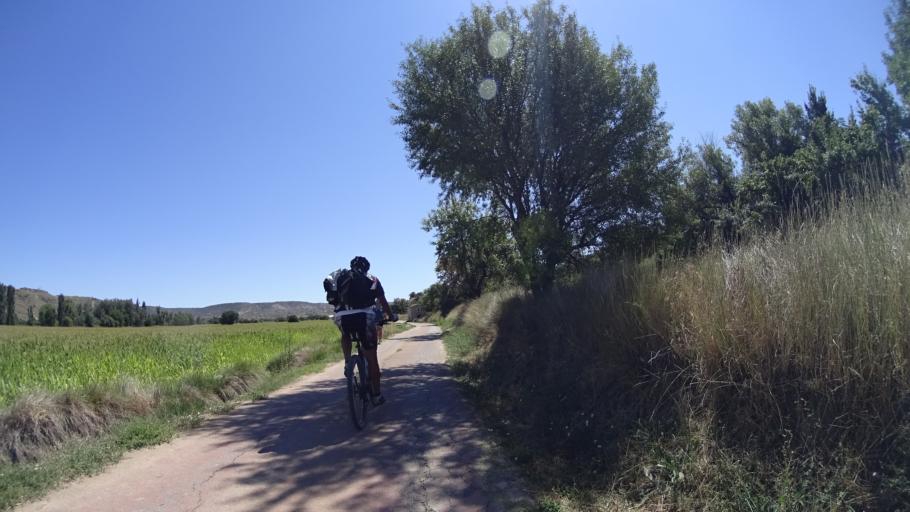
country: ES
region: Madrid
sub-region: Provincia de Madrid
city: Carabana
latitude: 40.2405
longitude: -3.2585
